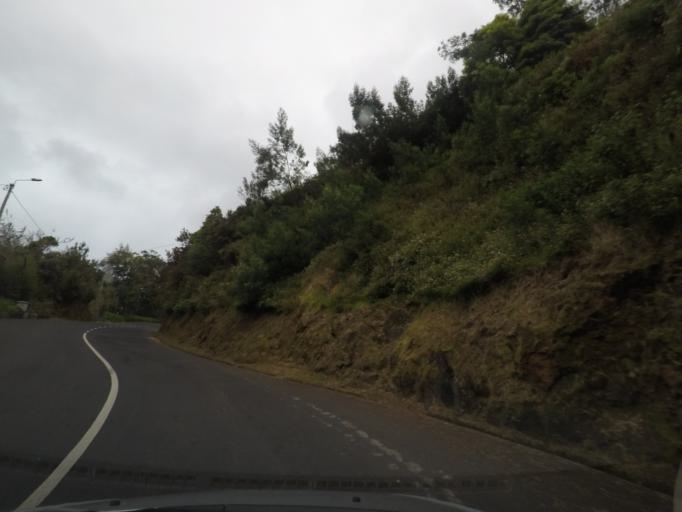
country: PT
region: Madeira
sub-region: Santana
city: Santana
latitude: 32.7507
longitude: -16.8397
